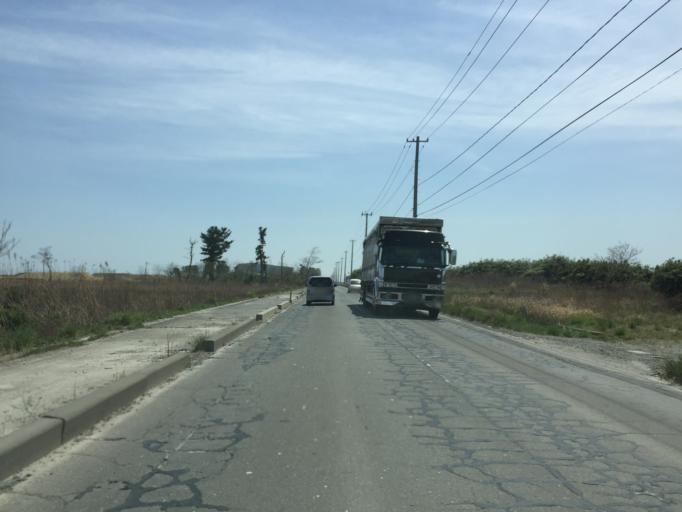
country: JP
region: Miyagi
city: Watari
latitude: 37.9668
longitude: 140.9074
